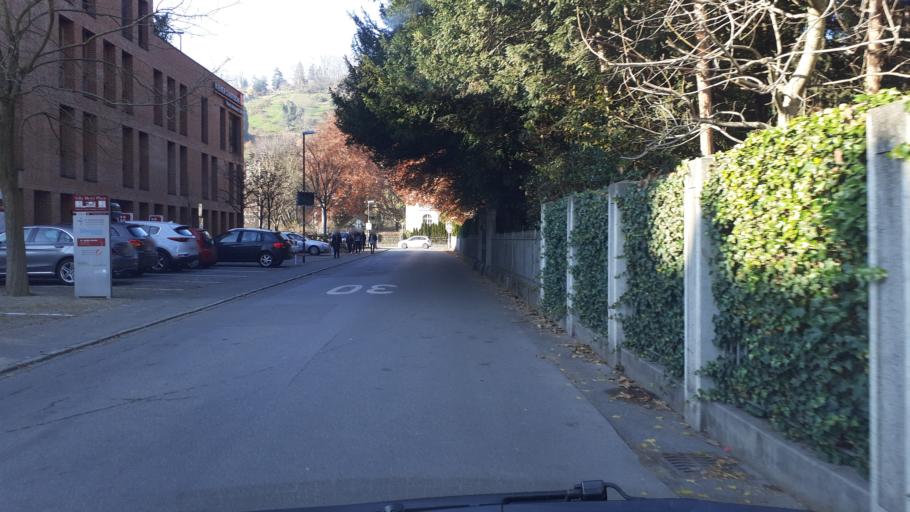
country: AT
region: Vorarlberg
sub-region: Politischer Bezirk Feldkirch
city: Feldkirch
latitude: 47.2402
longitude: 9.6020
